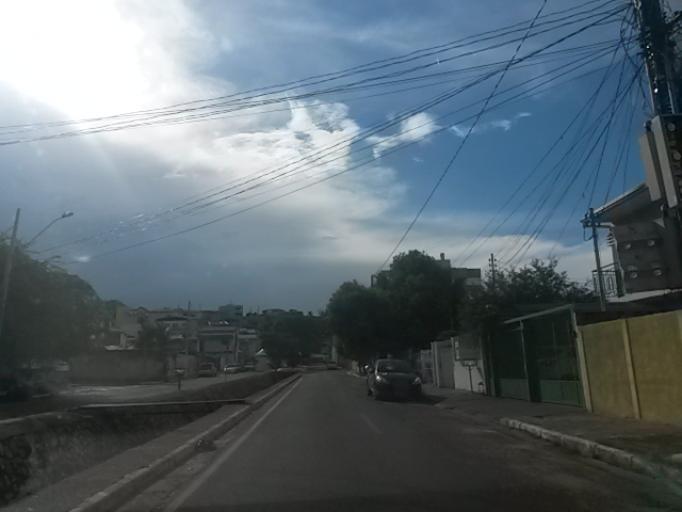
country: BR
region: Mato Grosso
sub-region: Cuiaba
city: Cuiaba
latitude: -15.5989
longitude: -56.0807
